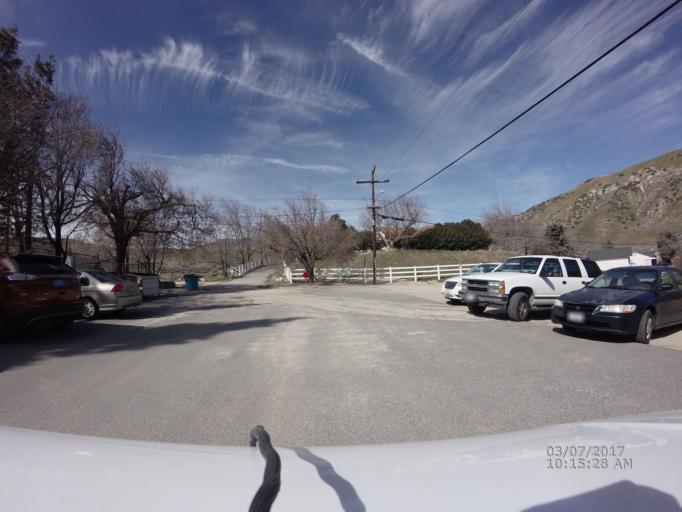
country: US
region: California
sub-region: Kern County
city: Lebec
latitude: 34.7931
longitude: -118.8540
